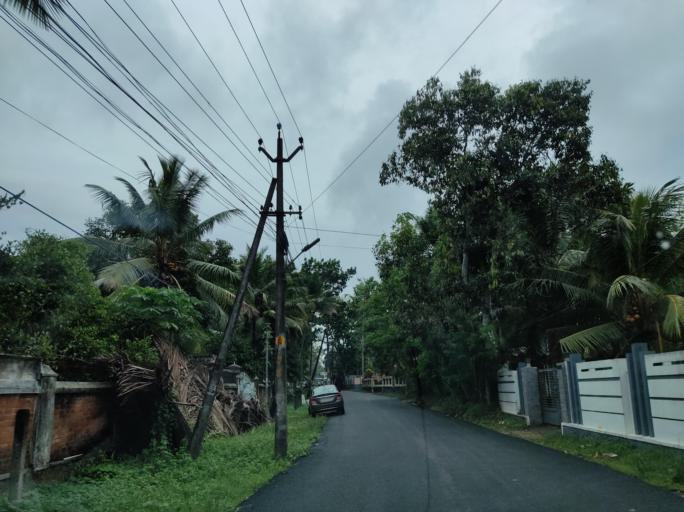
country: IN
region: Kerala
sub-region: Alappuzha
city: Mavelikara
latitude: 9.2449
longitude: 76.5281
